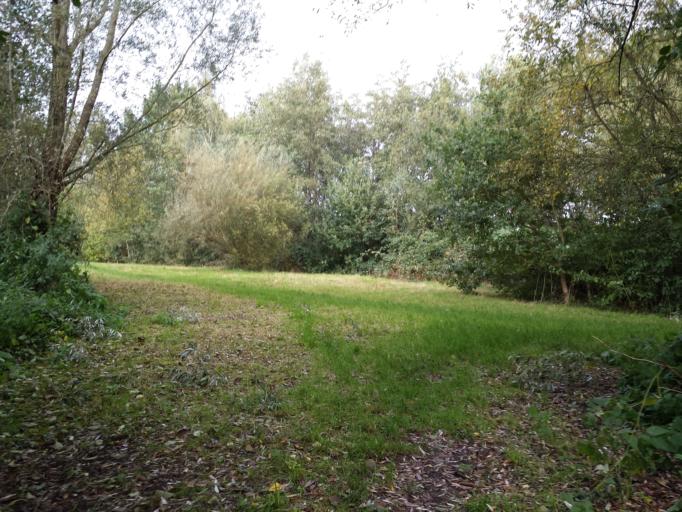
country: NL
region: Utrecht
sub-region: Gemeente De Bilt
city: De Bilt
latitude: 52.1108
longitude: 5.1694
